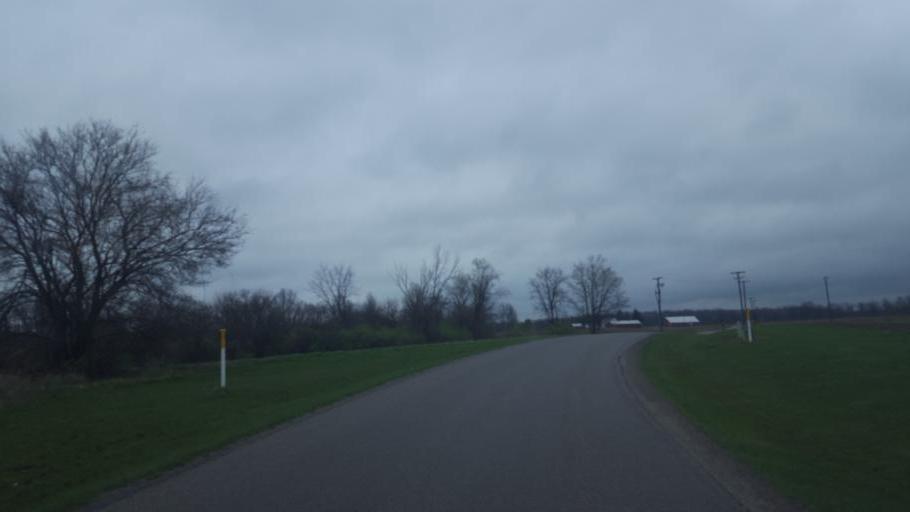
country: US
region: Ohio
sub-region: Morrow County
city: Mount Gilead
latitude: 40.5251
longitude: -82.8581
